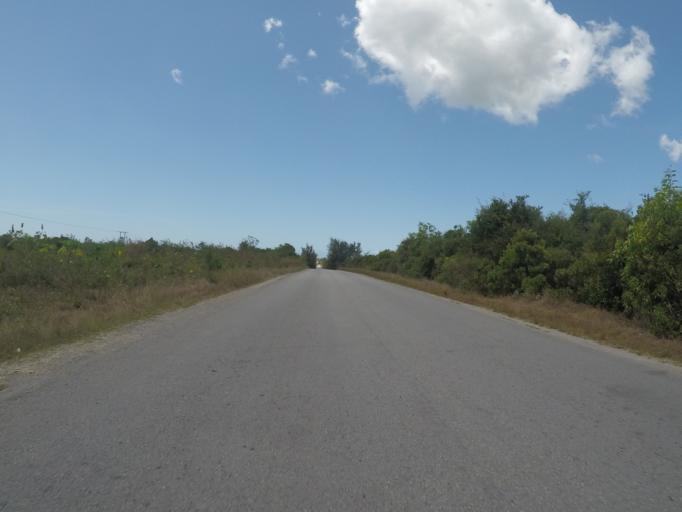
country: TZ
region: Zanzibar Central/South
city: Nganane
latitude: -6.2816
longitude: 39.4730
